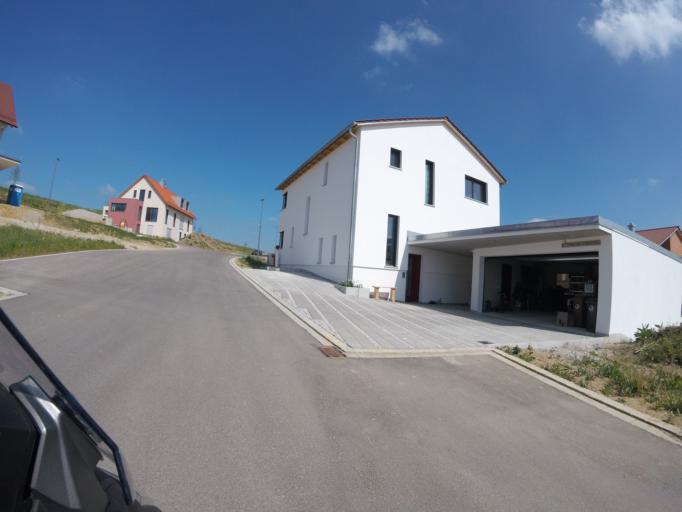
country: DE
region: Bavaria
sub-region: Upper Bavaria
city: Jetzendorf
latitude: 48.4378
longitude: 11.4233
